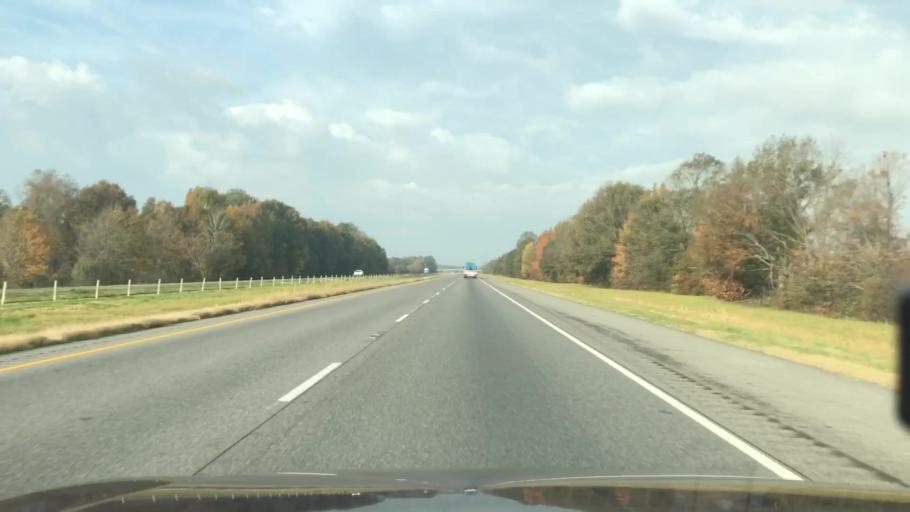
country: US
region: Louisiana
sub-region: Richland Parish
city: Delhi
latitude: 32.4236
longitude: -91.3539
